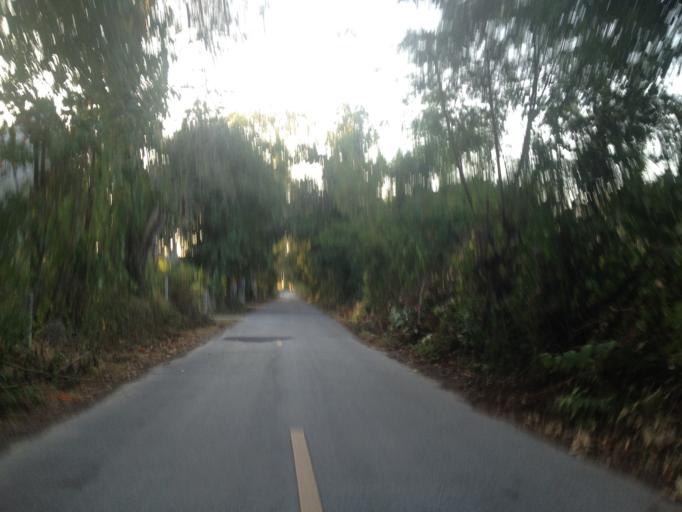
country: TH
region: Chiang Mai
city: Hang Dong
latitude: 18.6805
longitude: 98.8809
